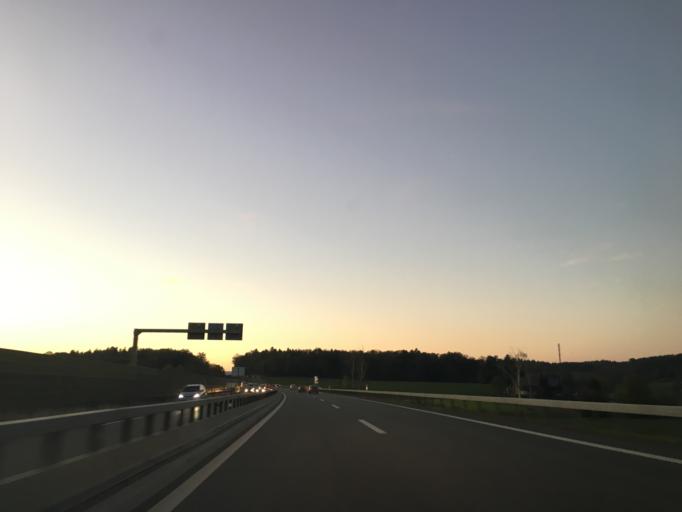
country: CH
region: Zurich
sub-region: Bezirk Andelfingen
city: Kleinandelfingen
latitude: 47.6237
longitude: 8.6805
